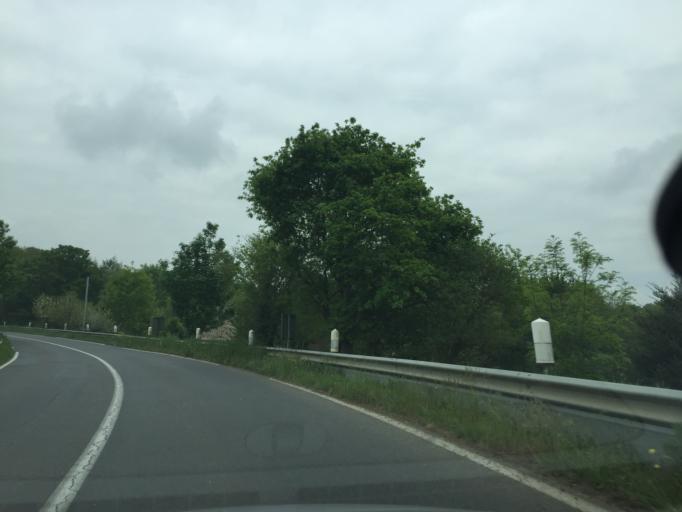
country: FR
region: Brittany
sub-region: Departement des Cotes-d'Armor
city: Henanbihen
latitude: 48.5738
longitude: -2.3642
